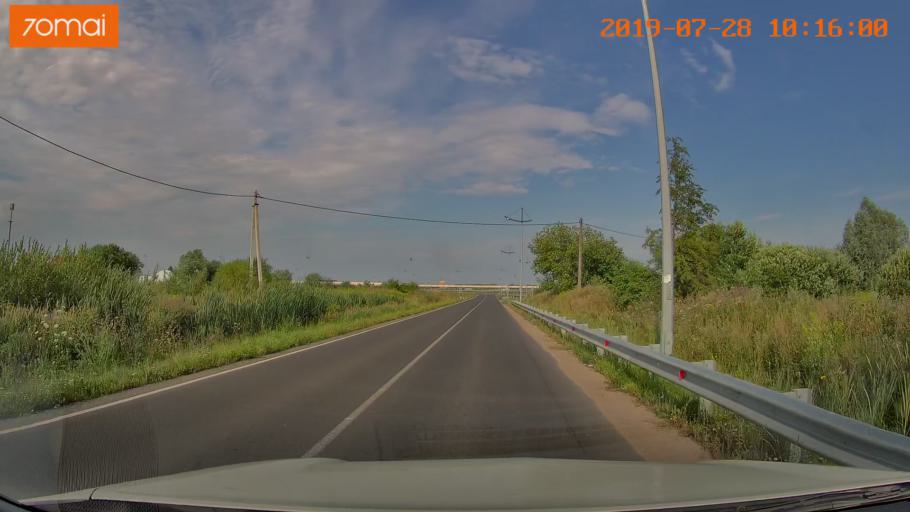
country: RU
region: Kaliningrad
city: Bol'shoe Isakovo
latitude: 54.7254
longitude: 20.6010
